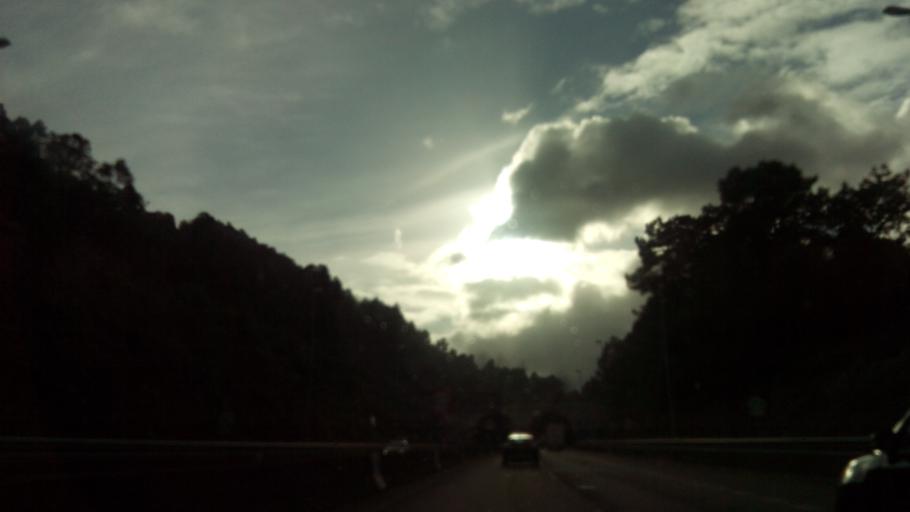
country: ES
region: Galicia
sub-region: Provincia de Pontevedra
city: Vigo
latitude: 42.2557
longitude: -8.6760
